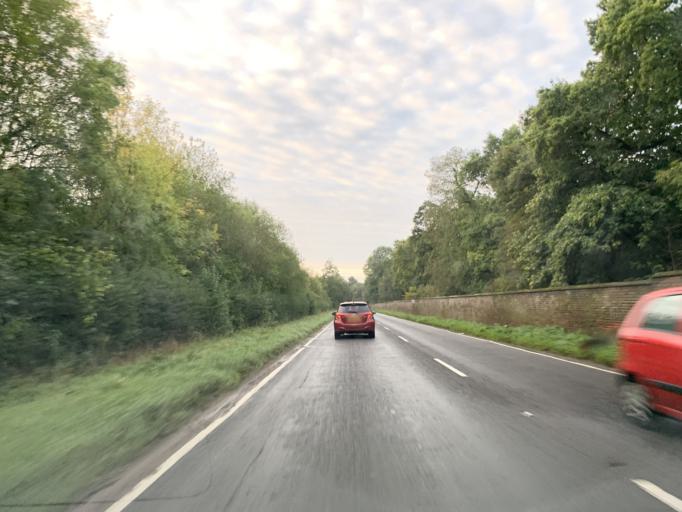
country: GB
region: England
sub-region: Hampshire
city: Romsey
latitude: 50.9809
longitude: -1.4863
